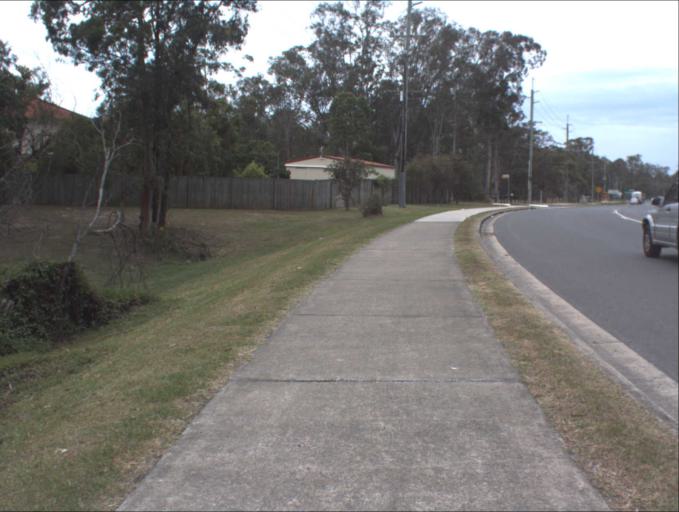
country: AU
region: Queensland
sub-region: Logan
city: Beenleigh
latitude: -27.6644
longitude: 153.2084
